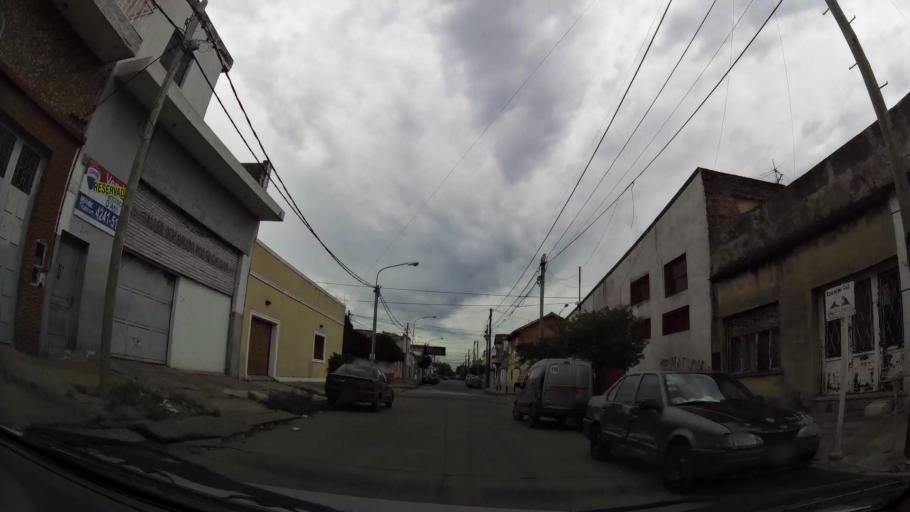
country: AR
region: Buenos Aires
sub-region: Partido de Lanus
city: Lanus
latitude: -34.6774
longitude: -58.3955
